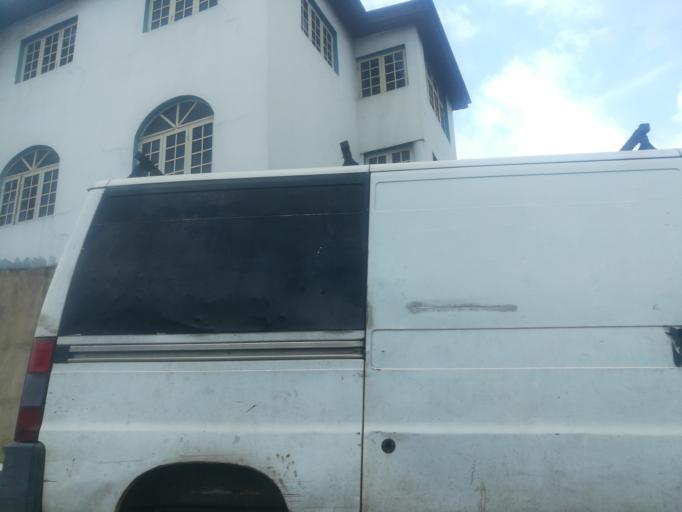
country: NG
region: Lagos
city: Somolu
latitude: 6.5580
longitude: 3.3939
